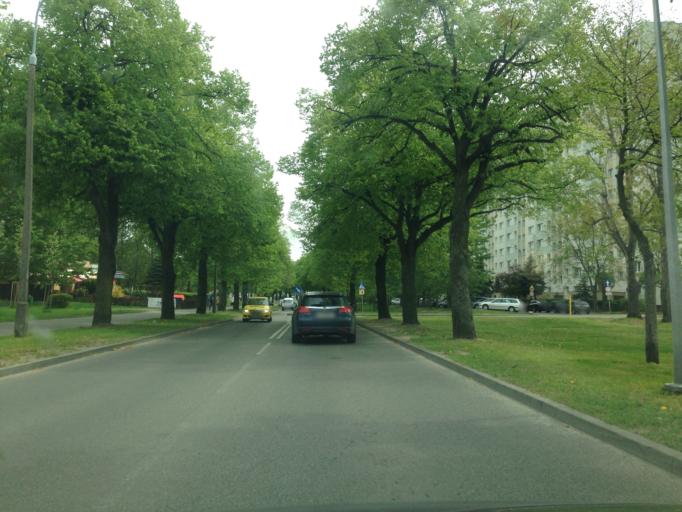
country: PL
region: Pomeranian Voivodeship
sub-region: Sopot
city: Sopot
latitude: 54.4228
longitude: 18.5796
